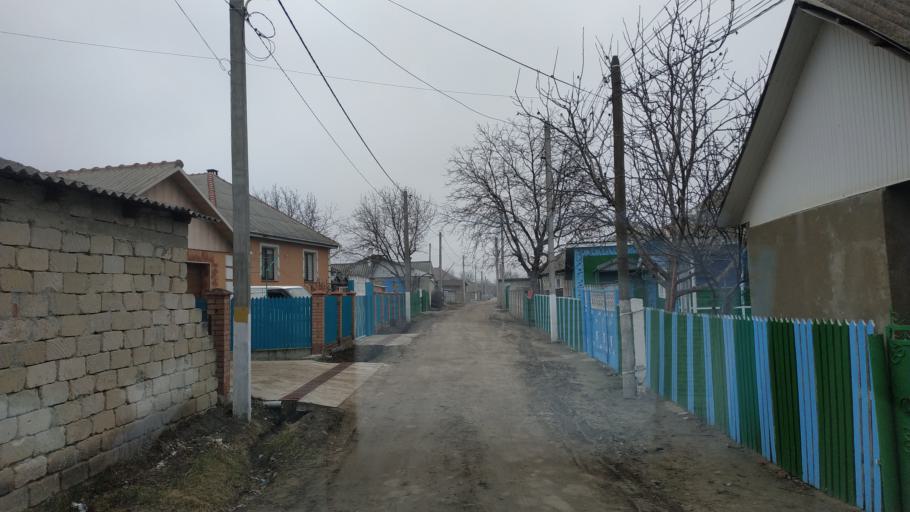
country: MD
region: Hincesti
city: Hincesti
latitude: 46.8929
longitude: 28.5461
